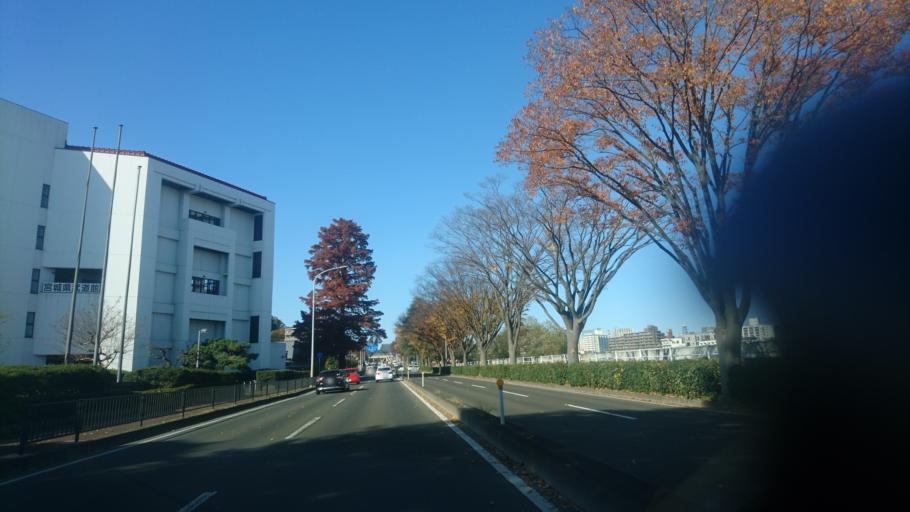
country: JP
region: Miyagi
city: Sendai
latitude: 38.2377
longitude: 140.8864
